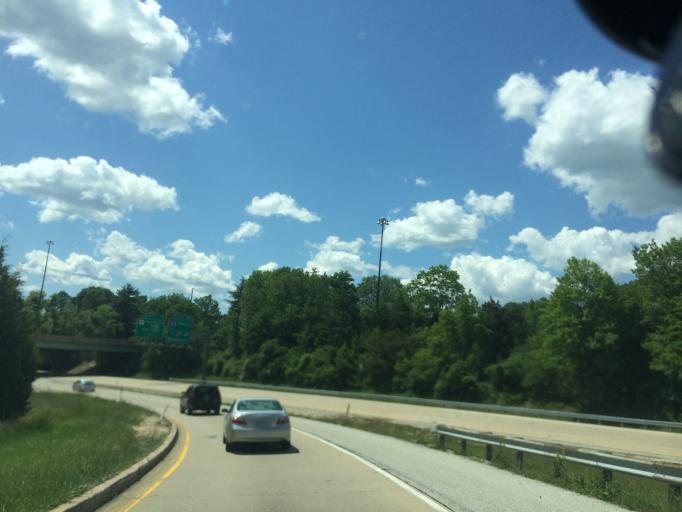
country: US
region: Maryland
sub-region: Baltimore County
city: Arbutus
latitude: 39.2365
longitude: -76.7111
